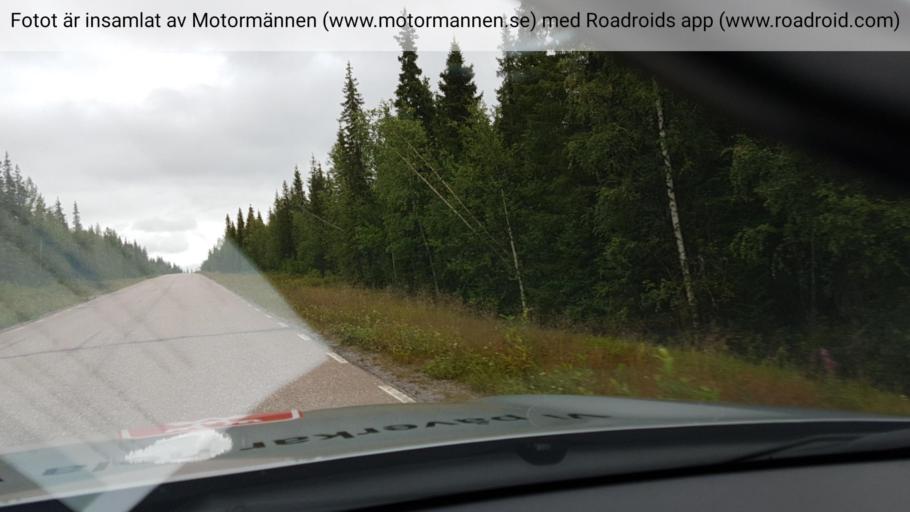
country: SE
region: Norrbotten
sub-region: Overkalix Kommun
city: OEverkalix
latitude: 67.0392
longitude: 22.0359
